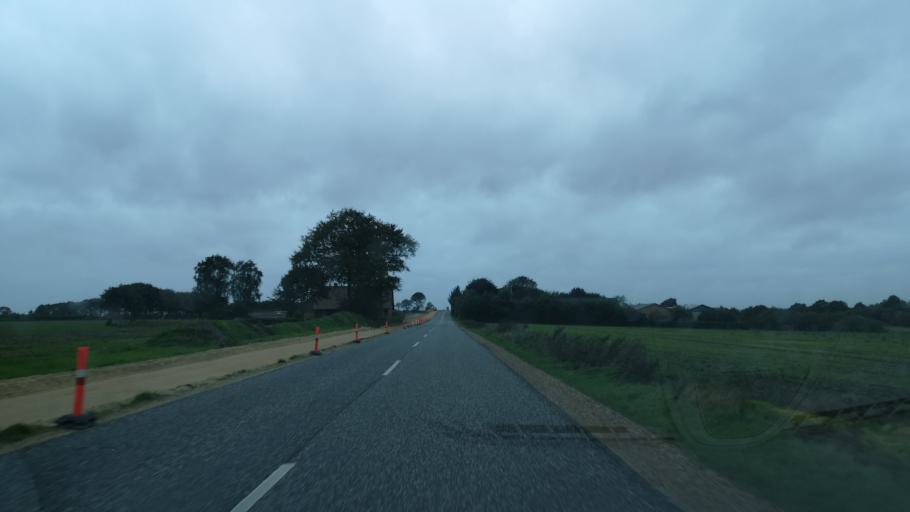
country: DK
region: Central Jutland
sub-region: Ringkobing-Skjern Kommune
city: Videbaek
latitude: 56.0532
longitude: 8.6464
